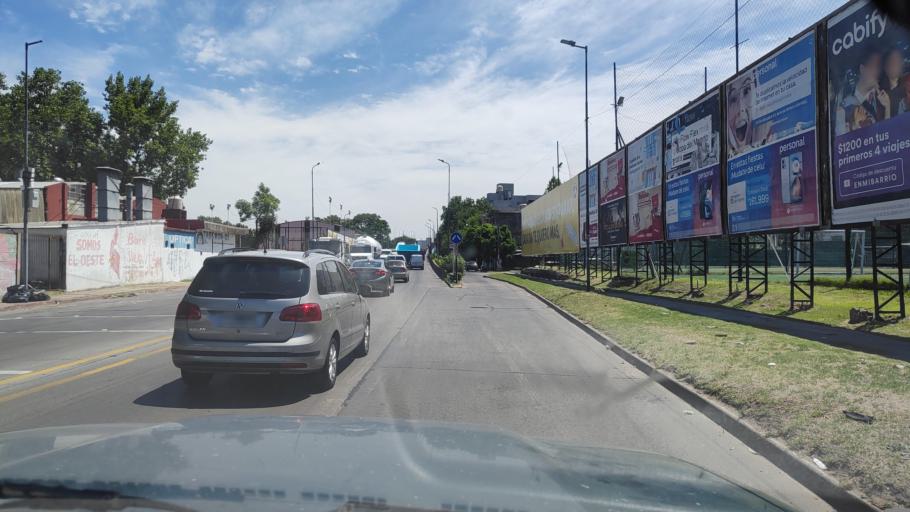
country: AR
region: Buenos Aires
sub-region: Partido de Moron
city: Moron
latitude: -34.6521
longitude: -58.6296
